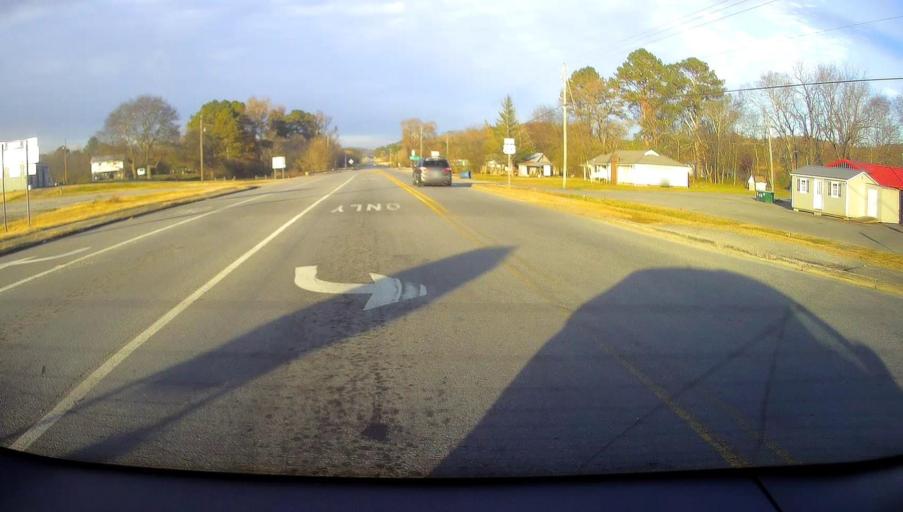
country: US
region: Alabama
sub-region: Blount County
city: Blountsville
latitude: 34.1669
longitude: -86.5164
